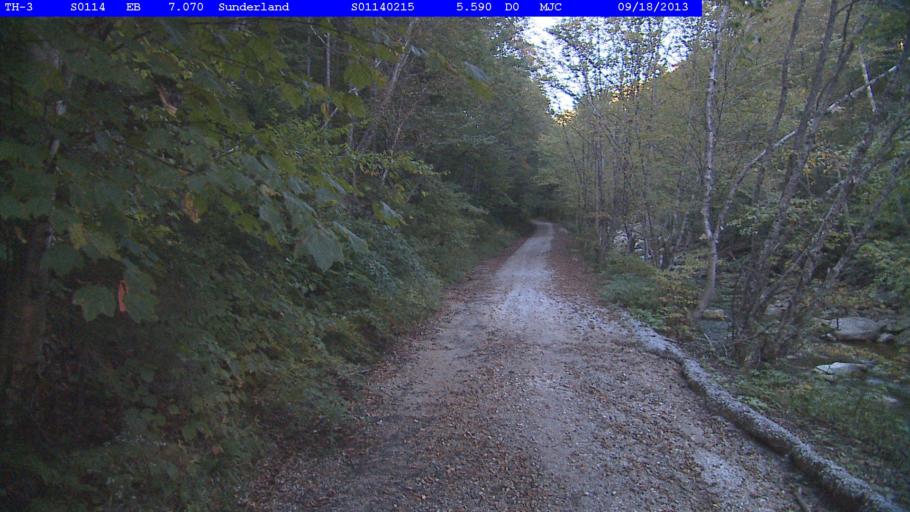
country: US
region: Vermont
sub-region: Bennington County
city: Arlington
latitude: 43.0561
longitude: -73.0703
